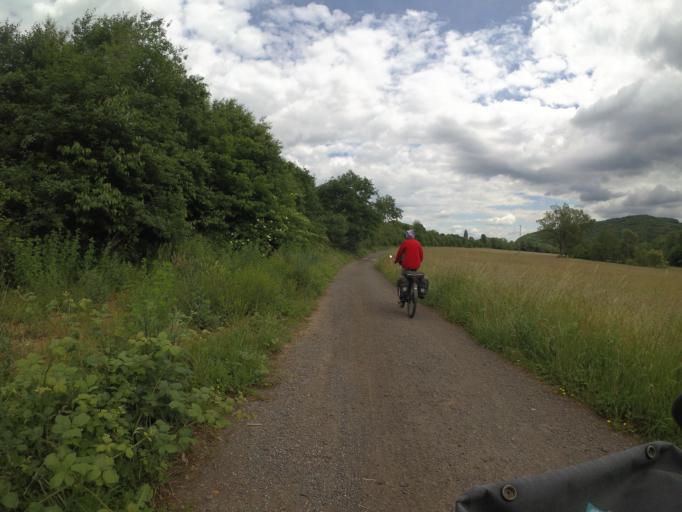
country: DE
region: Rheinland-Pfalz
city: Rathsweiler
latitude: 49.5956
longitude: 7.4581
